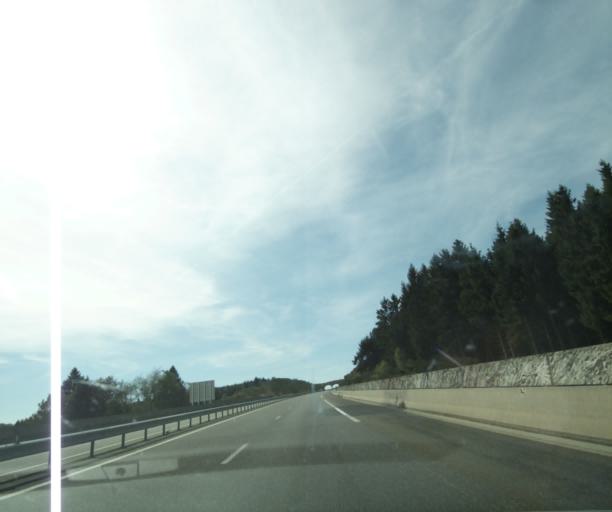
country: FR
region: Auvergne
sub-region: Departement du Puy-de-Dome
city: Charbonnieres-les-Varennes
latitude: 45.9088
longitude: 2.9525
